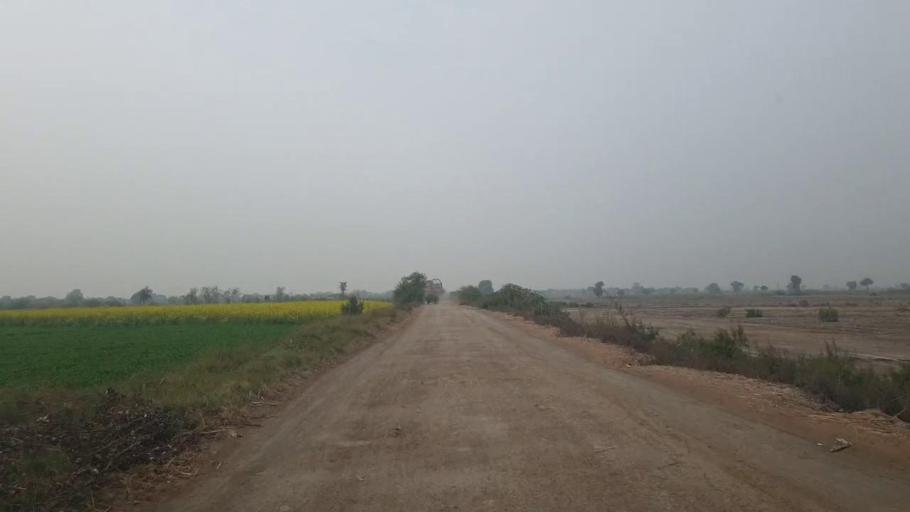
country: PK
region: Sindh
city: Tando Adam
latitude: 25.8073
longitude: 68.7201
